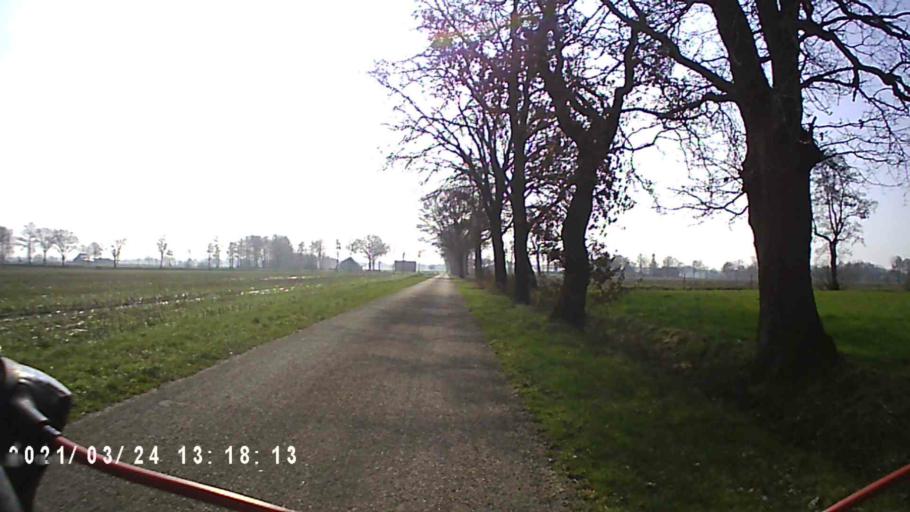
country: NL
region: Groningen
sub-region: Gemeente Leek
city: Leek
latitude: 53.1073
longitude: 6.2933
